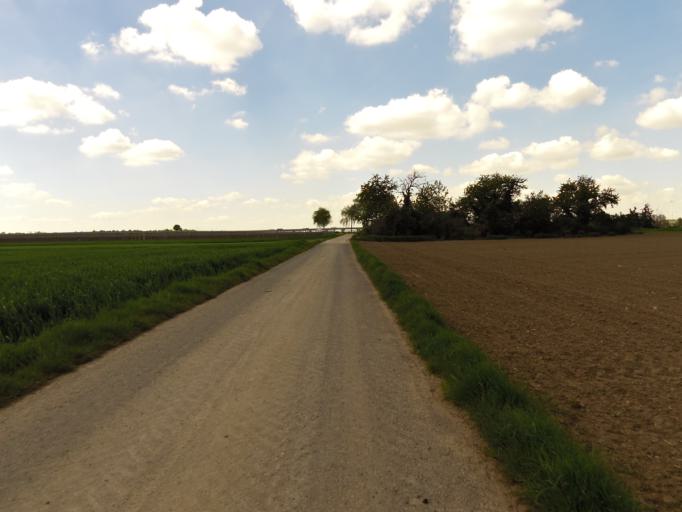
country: DE
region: Rheinland-Pfalz
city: Kleinniedesheim
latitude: 49.6304
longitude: 8.3124
